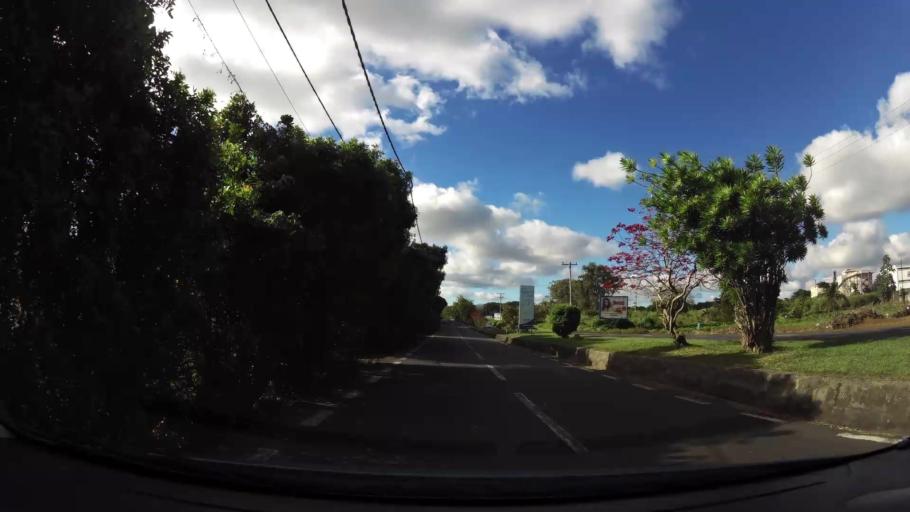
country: MU
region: Plaines Wilhems
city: Vacoas
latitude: -20.2862
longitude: 57.4966
